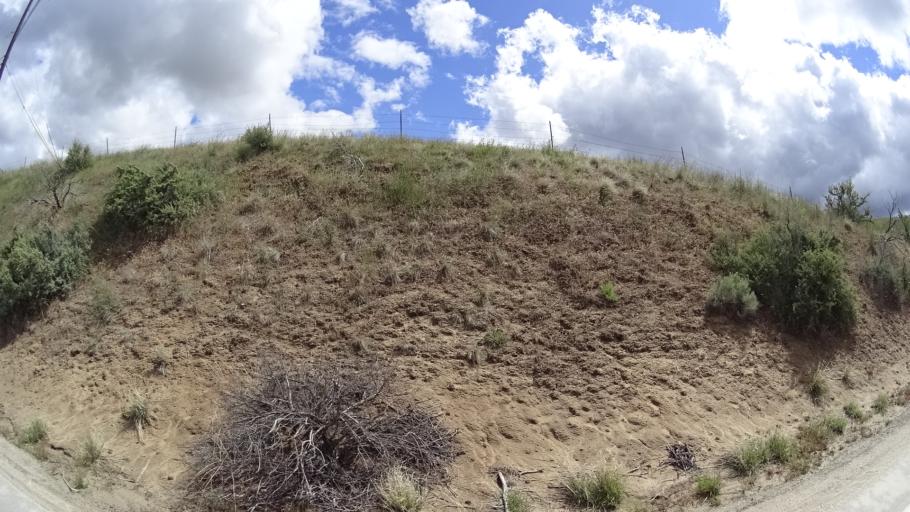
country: US
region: Idaho
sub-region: Ada County
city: Boise
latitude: 43.6737
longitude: -116.1806
